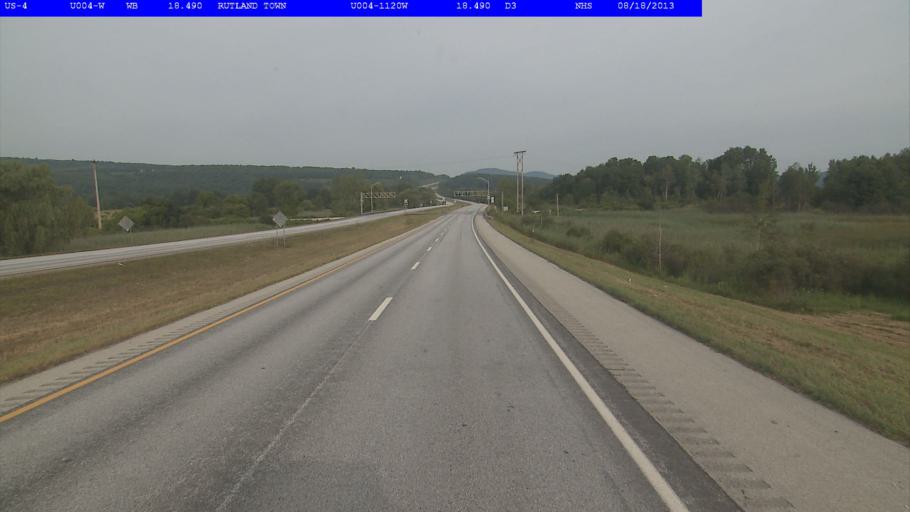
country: US
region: Vermont
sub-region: Rutland County
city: Rutland
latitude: 43.5803
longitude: -72.9730
